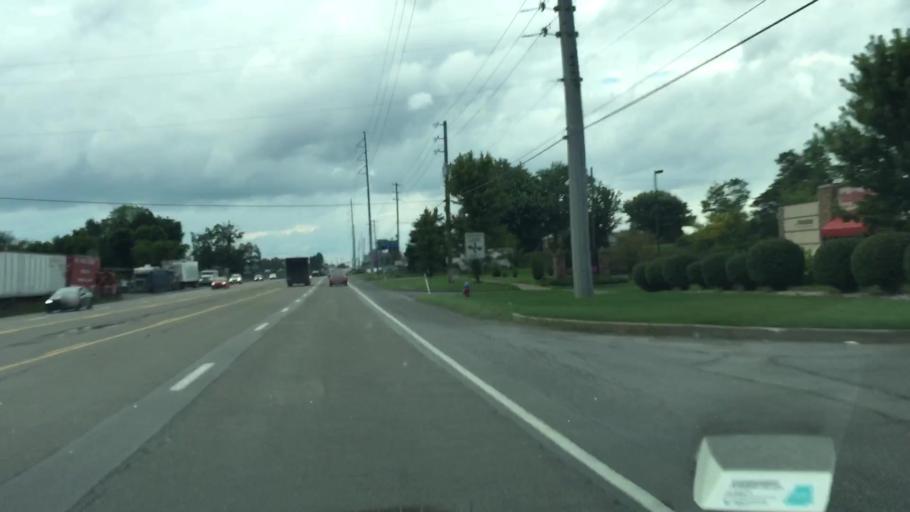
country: US
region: Pennsylvania
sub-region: Butler County
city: Fox Run
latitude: 40.7438
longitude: -80.1131
